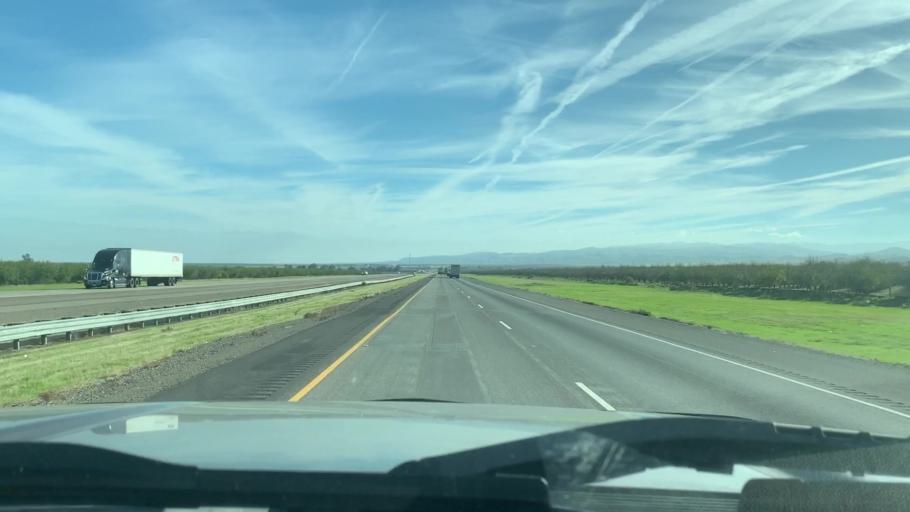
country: US
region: California
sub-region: Fresno County
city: Firebaugh
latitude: 36.6705
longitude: -120.6468
